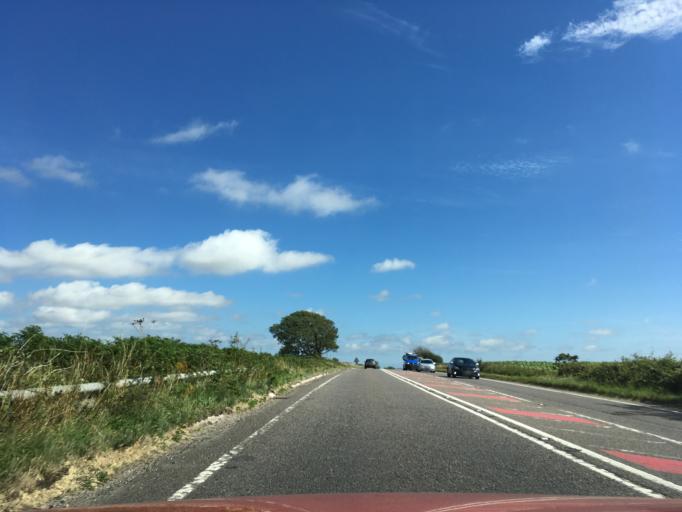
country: GB
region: England
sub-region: Dorset
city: Dorchester
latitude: 50.7701
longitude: -2.5368
